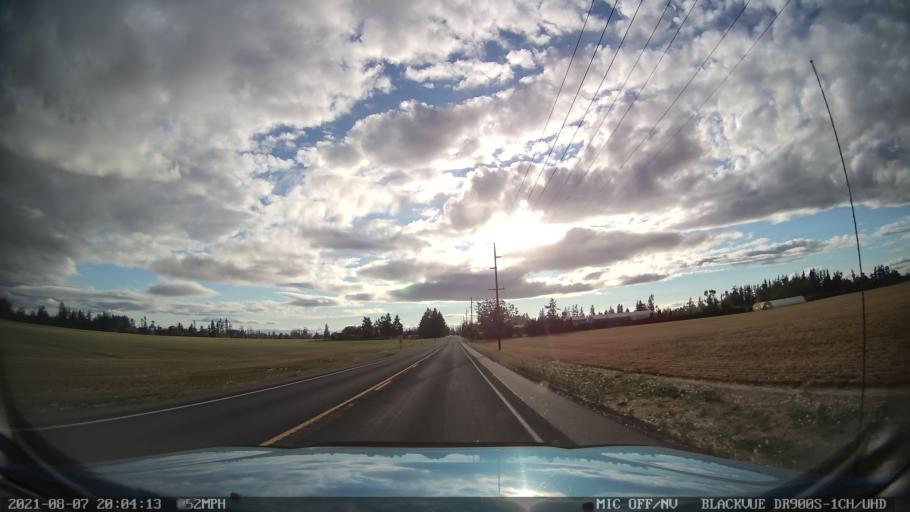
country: US
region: Oregon
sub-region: Marion County
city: Silverton
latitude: 44.9942
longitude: -122.8290
